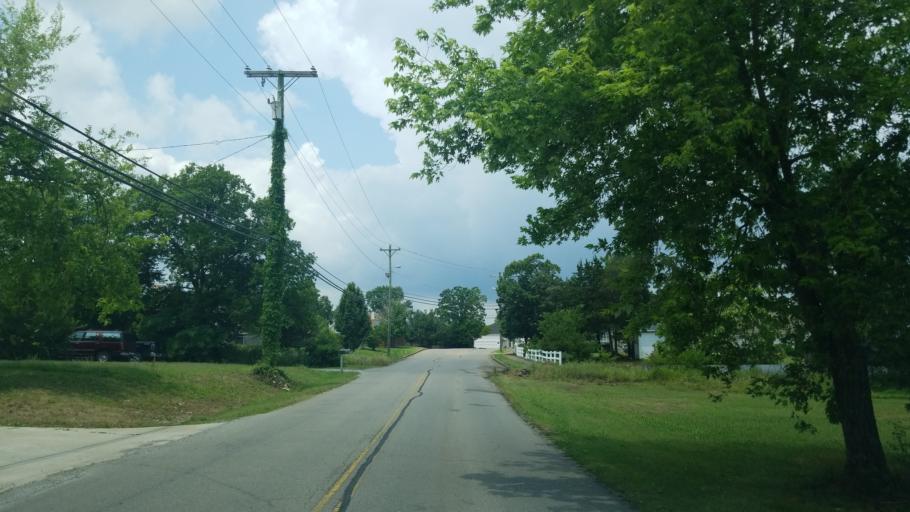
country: US
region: Tennessee
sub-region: Rutherford County
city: La Vergne
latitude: 36.0470
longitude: -86.5885
